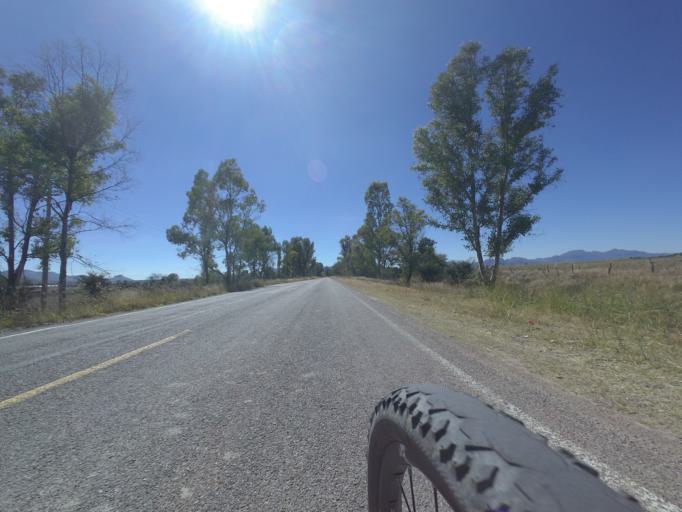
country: MX
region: Aguascalientes
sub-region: Aguascalientes
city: Los Canos
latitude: 21.8806
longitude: -102.4936
